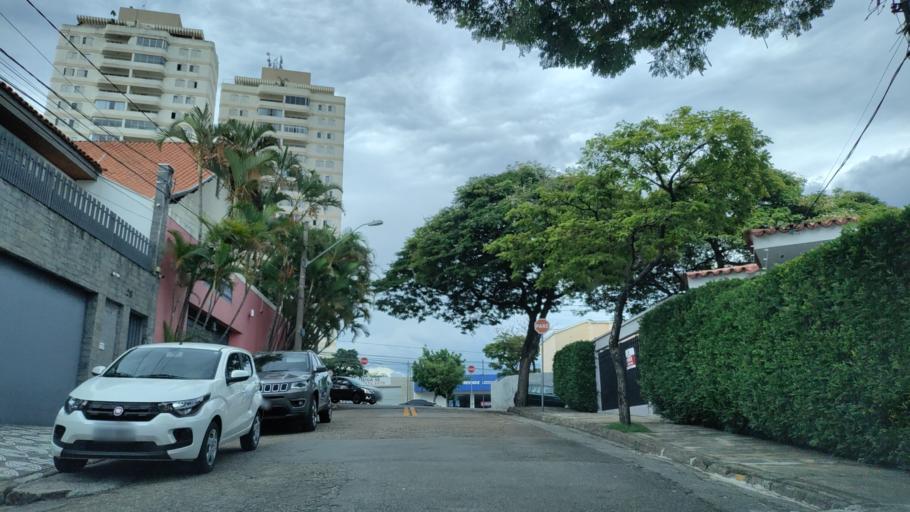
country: BR
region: Sao Paulo
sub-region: Sorocaba
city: Sorocaba
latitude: -23.4932
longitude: -47.4687
